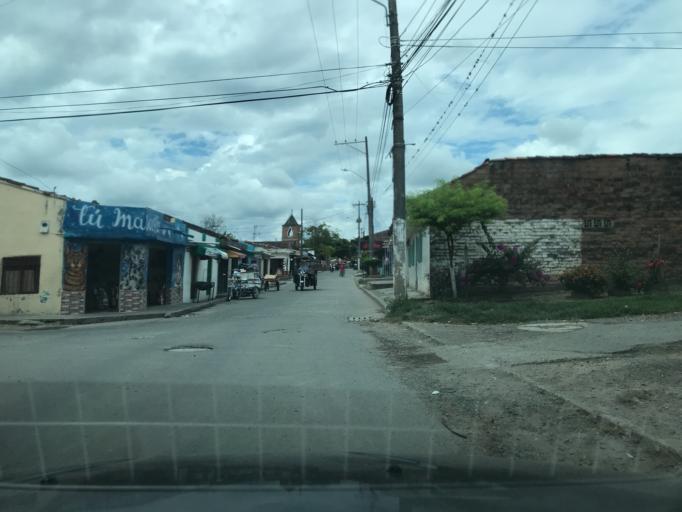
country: CO
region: Valle del Cauca
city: Cartago
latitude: 4.7610
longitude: -75.9338
